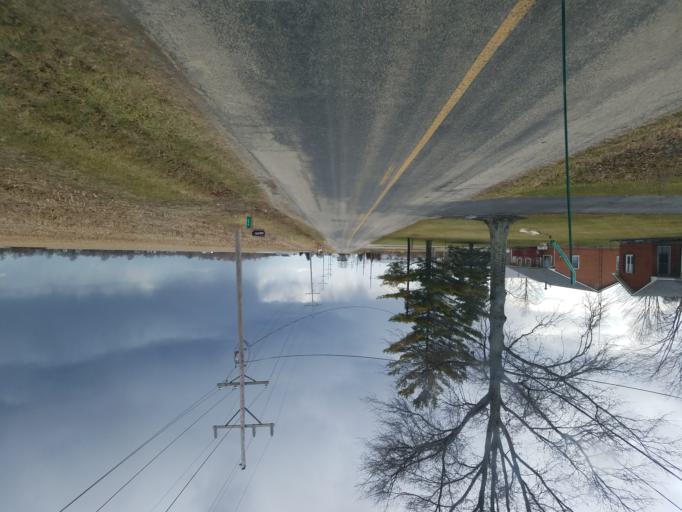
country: US
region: Ohio
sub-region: Marion County
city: Prospect
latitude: 40.4585
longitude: -83.0981
